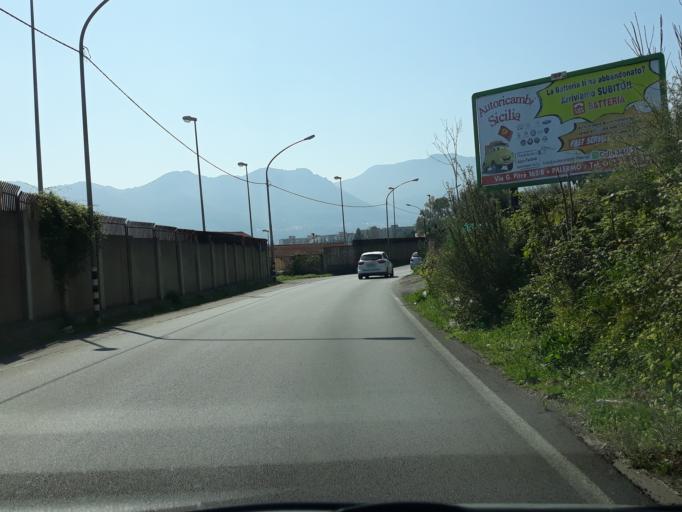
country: IT
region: Sicily
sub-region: Palermo
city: Monreale
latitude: 38.1023
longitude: 13.3104
